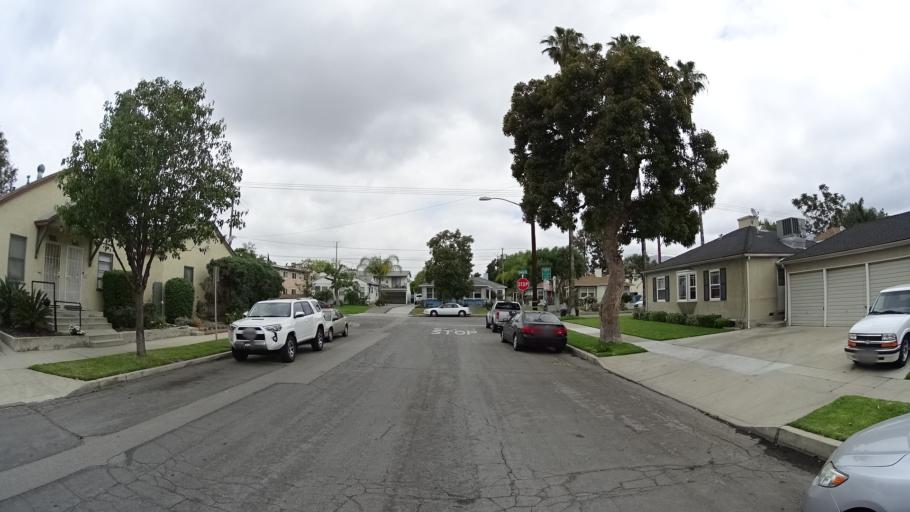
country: US
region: California
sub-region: Los Angeles County
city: Burbank
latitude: 34.1732
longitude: -118.3179
